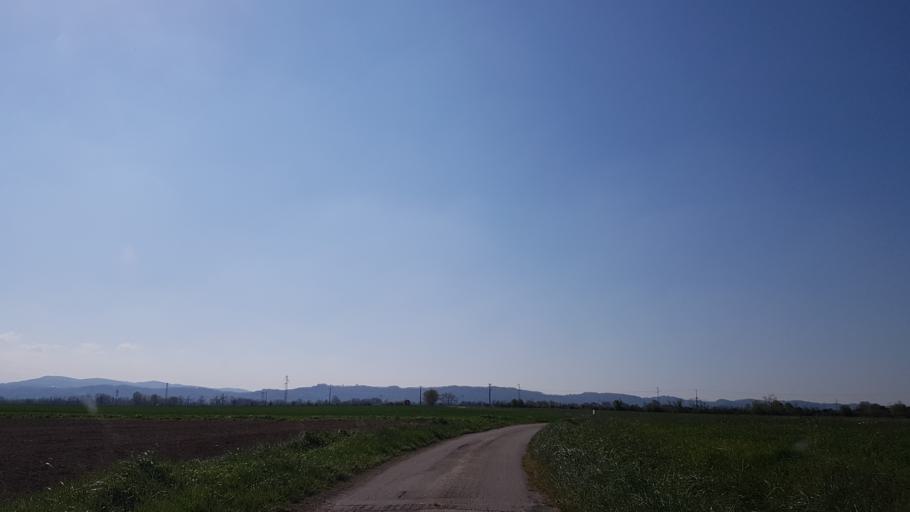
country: FR
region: Midi-Pyrenees
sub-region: Departement de l'Ariege
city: Verniolle
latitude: 43.0868
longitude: 1.6720
